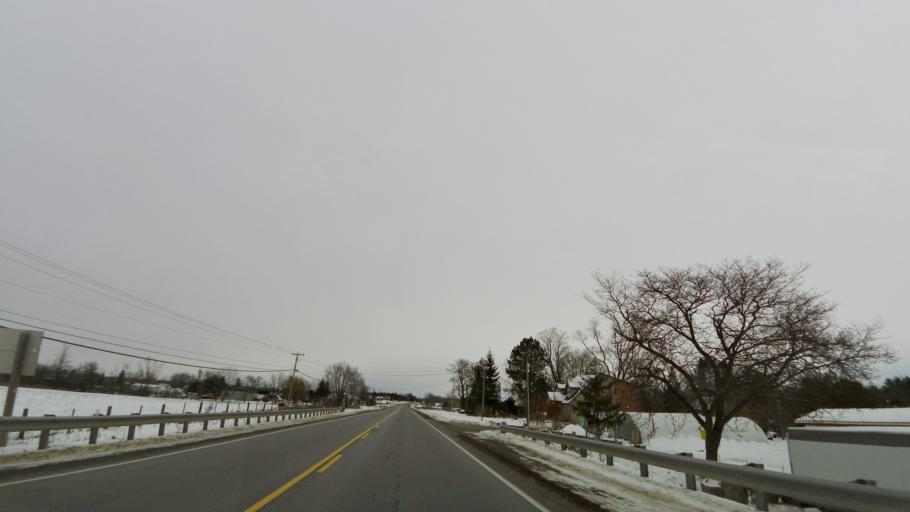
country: CA
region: Ontario
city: Cambridge
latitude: 43.3176
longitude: -80.1790
